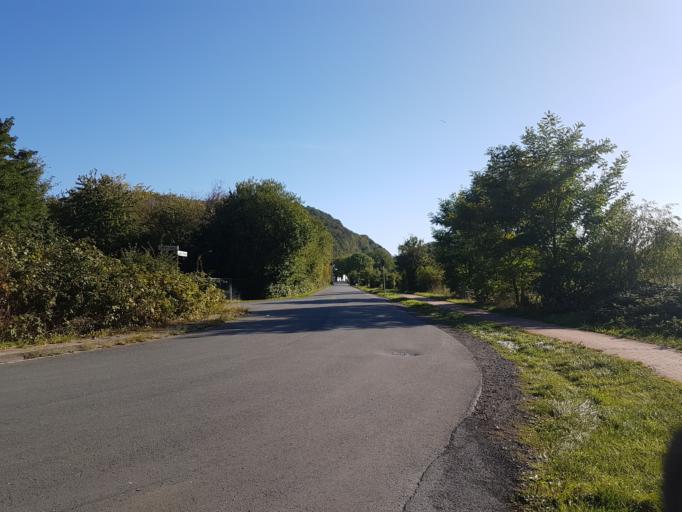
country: DE
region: North Rhine-Westphalia
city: Porta Westfalica
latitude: 52.2537
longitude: 8.9230
